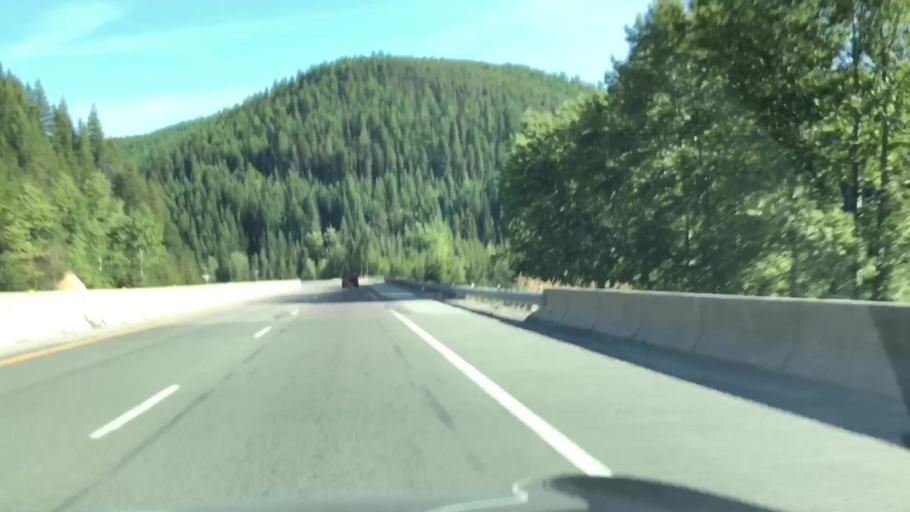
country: US
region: Montana
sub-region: Sanders County
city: Thompson Falls
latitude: 47.4175
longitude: -115.5902
